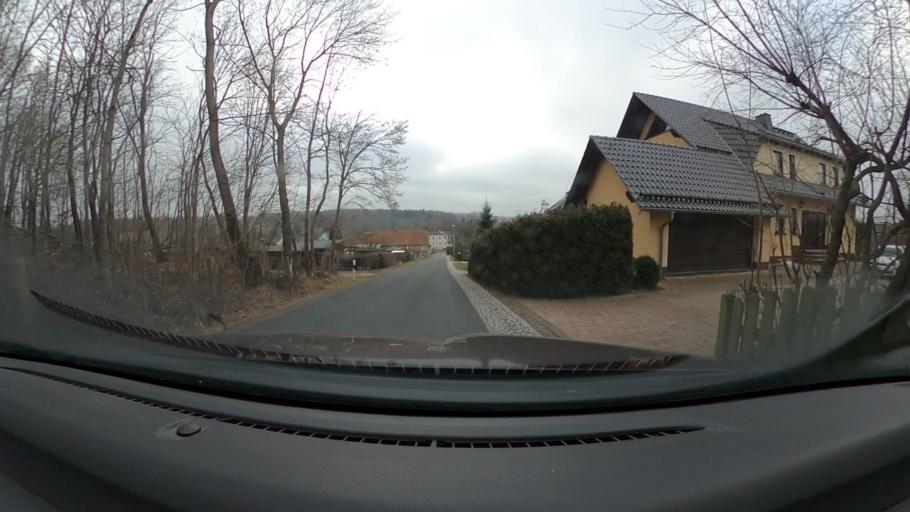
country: DE
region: Saxony
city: Oberschona
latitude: 50.9077
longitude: 13.2962
